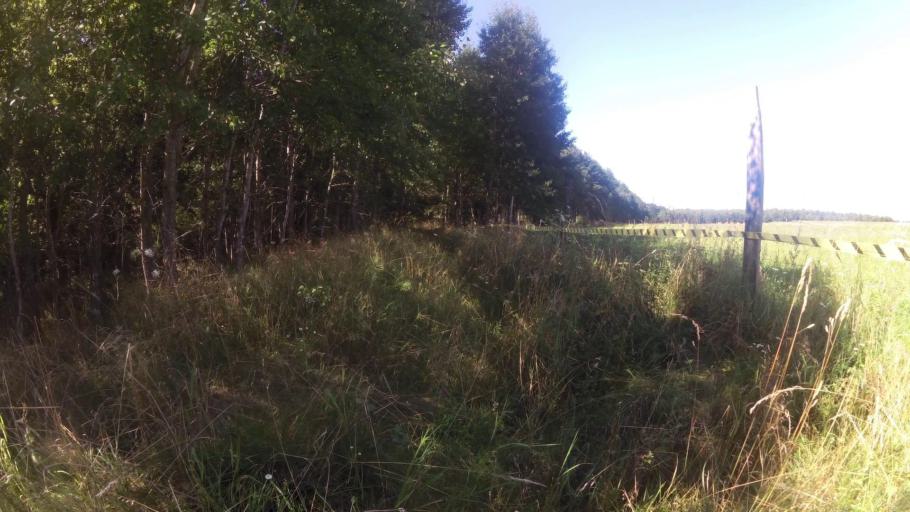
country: PL
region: West Pomeranian Voivodeship
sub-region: Powiat stargardzki
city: Insko
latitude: 53.4429
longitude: 15.6133
